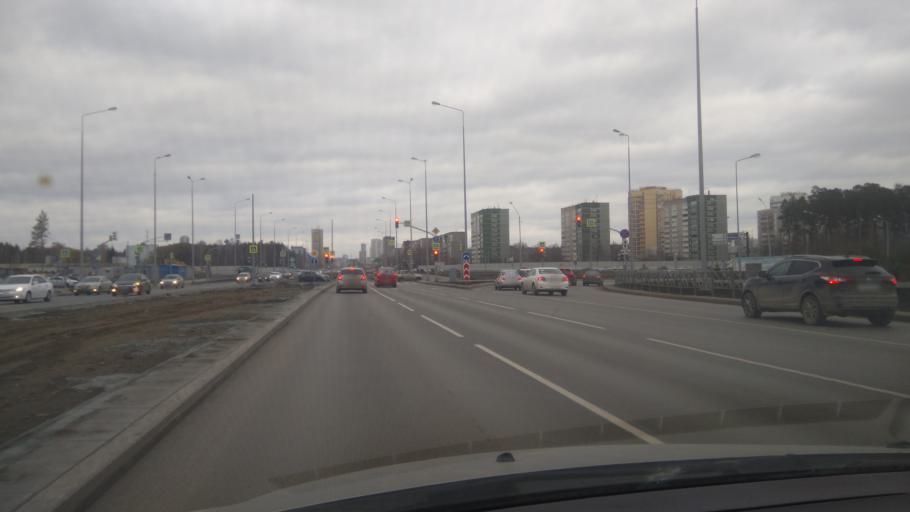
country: RU
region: Sverdlovsk
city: Sovkhoznyy
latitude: 56.8026
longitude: 60.5372
